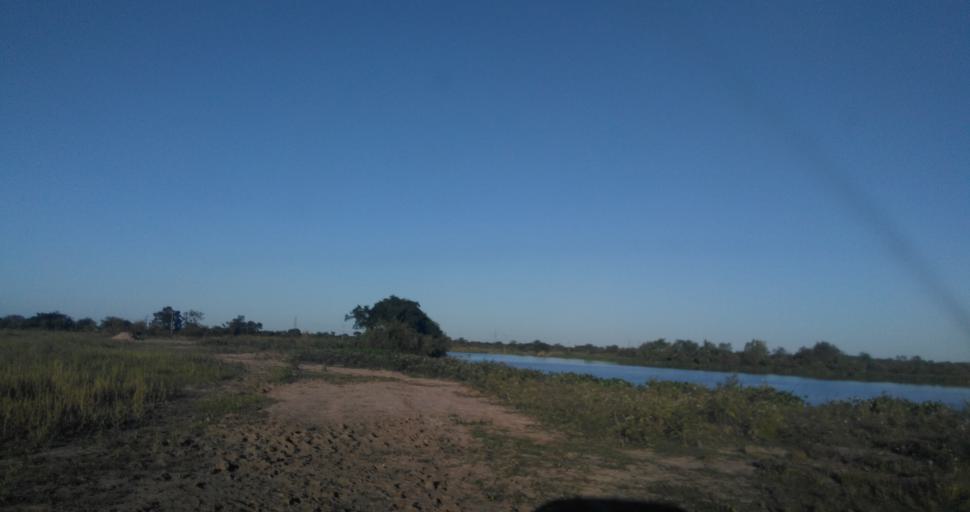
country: AR
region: Chaco
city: Fontana
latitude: -27.3944
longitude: -58.9829
